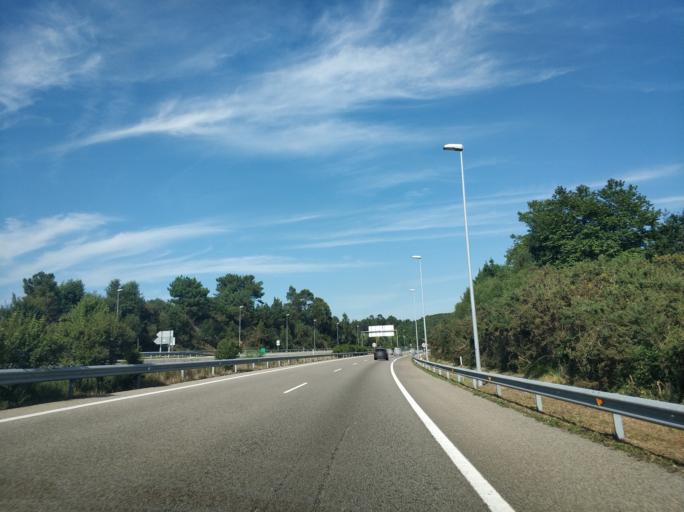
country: ES
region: Asturias
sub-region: Province of Asturias
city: Castrillon
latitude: 43.5492
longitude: -5.9972
